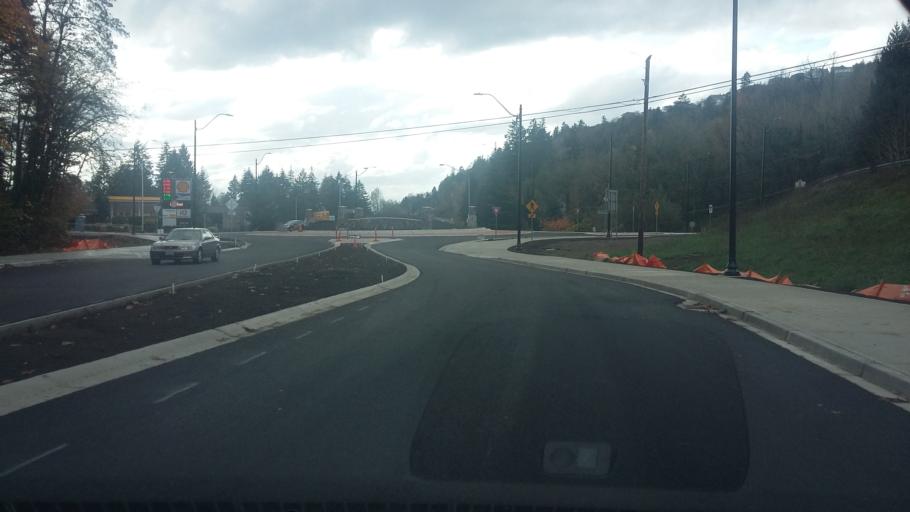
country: US
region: Washington
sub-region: Clark County
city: Camas
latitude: 45.5825
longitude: -122.4256
